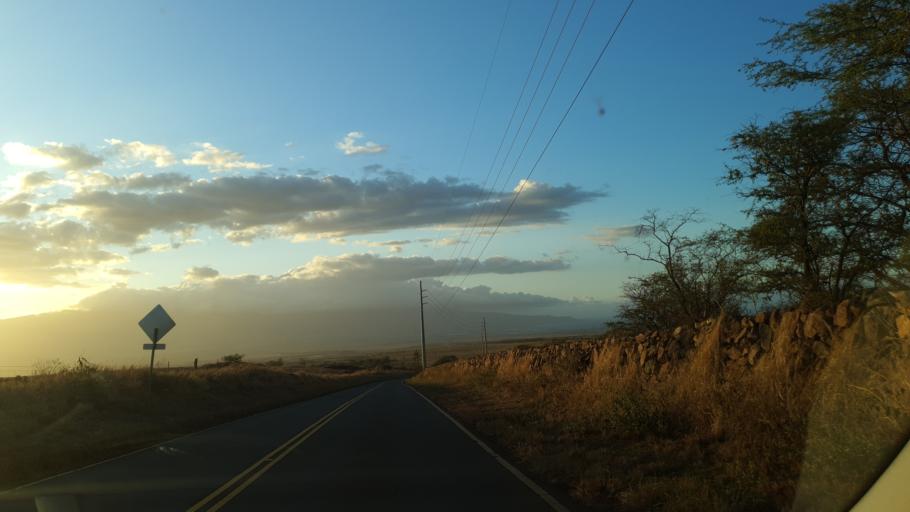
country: US
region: Hawaii
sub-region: Maui County
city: Pukalani
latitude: 20.7999
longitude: -156.3732
